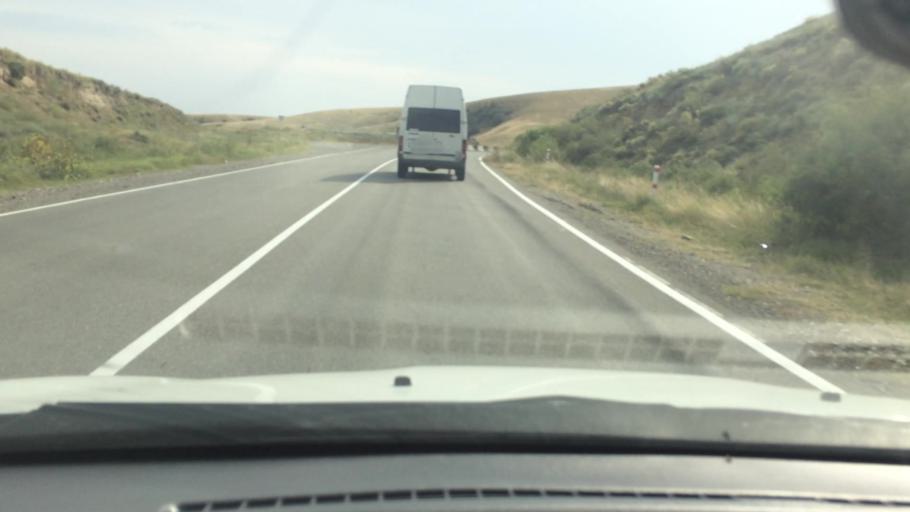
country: GE
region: Kvemo Kartli
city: Rust'avi
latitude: 41.5226
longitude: 44.9885
